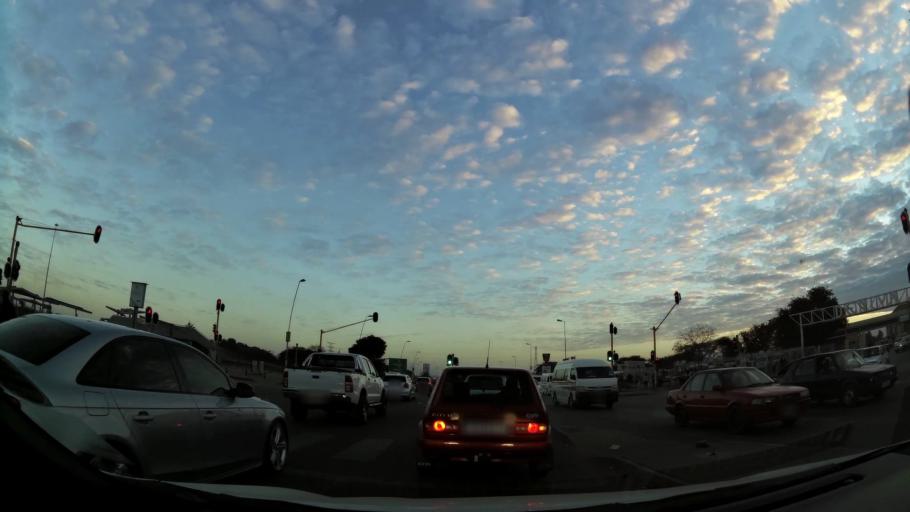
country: ZA
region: Gauteng
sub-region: City of Tshwane Metropolitan Municipality
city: Pretoria
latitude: -25.7145
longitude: 28.3355
